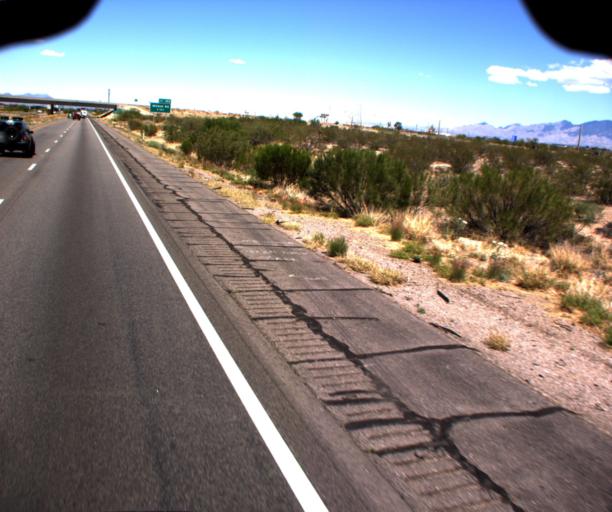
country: US
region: Arizona
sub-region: Pima County
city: Summit
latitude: 32.1022
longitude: -110.8381
